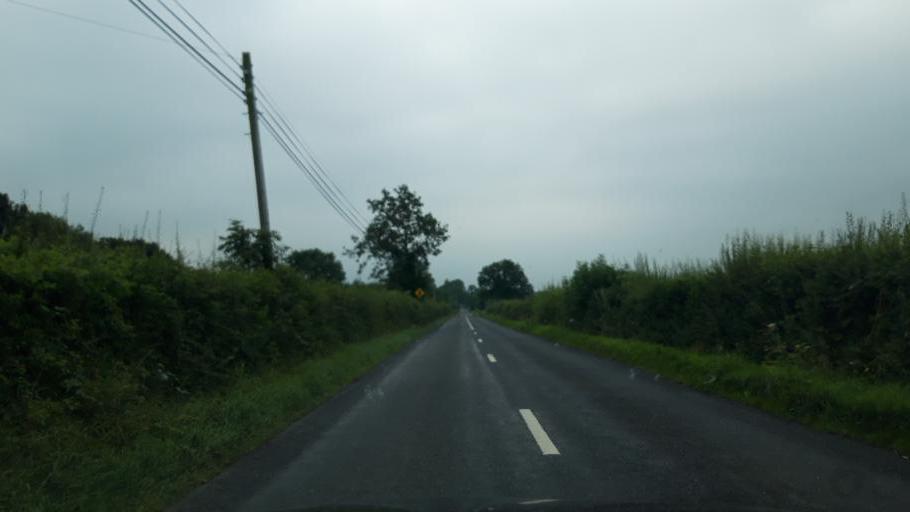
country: IE
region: Munster
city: Fethard
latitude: 52.5194
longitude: -7.6834
